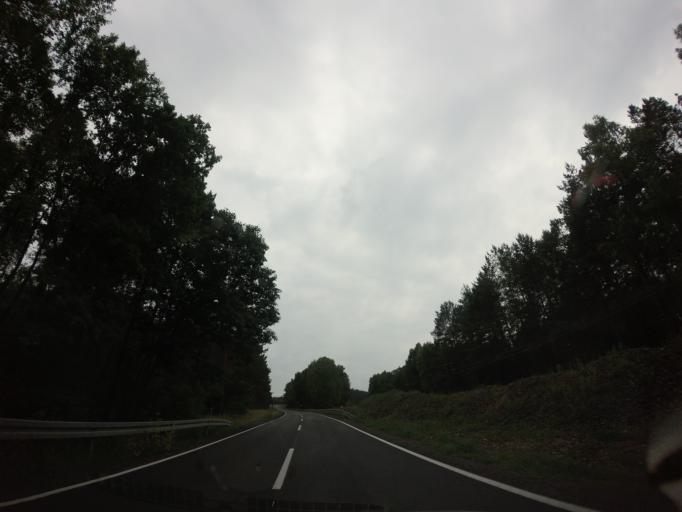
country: PL
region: West Pomeranian Voivodeship
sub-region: Powiat szczecinecki
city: Lubowo
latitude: 53.6049
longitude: 16.4410
